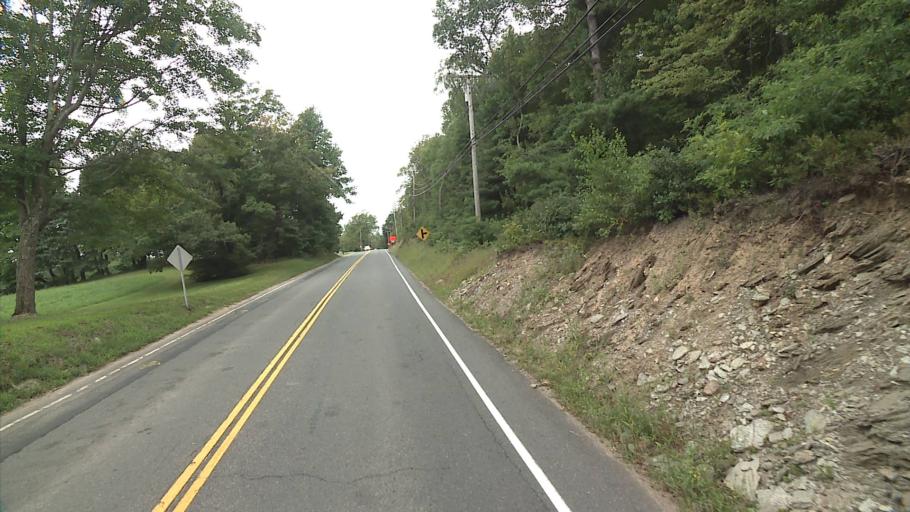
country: US
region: Connecticut
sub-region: Hartford County
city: Manchester
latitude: 41.7748
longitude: -72.4567
